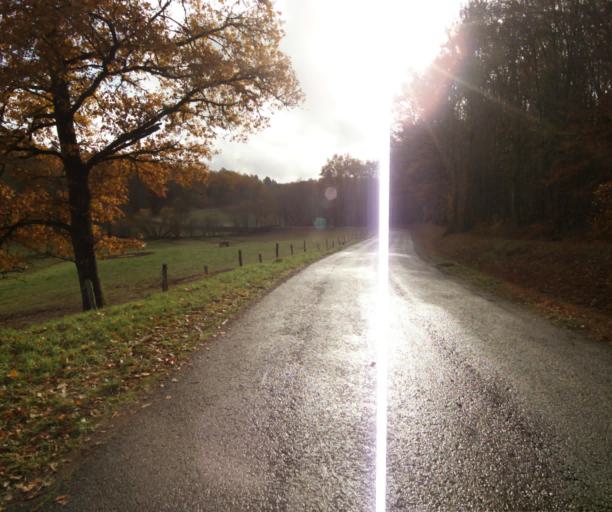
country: FR
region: Limousin
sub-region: Departement de la Correze
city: Saint-Mexant
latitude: 45.2349
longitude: 1.6414
